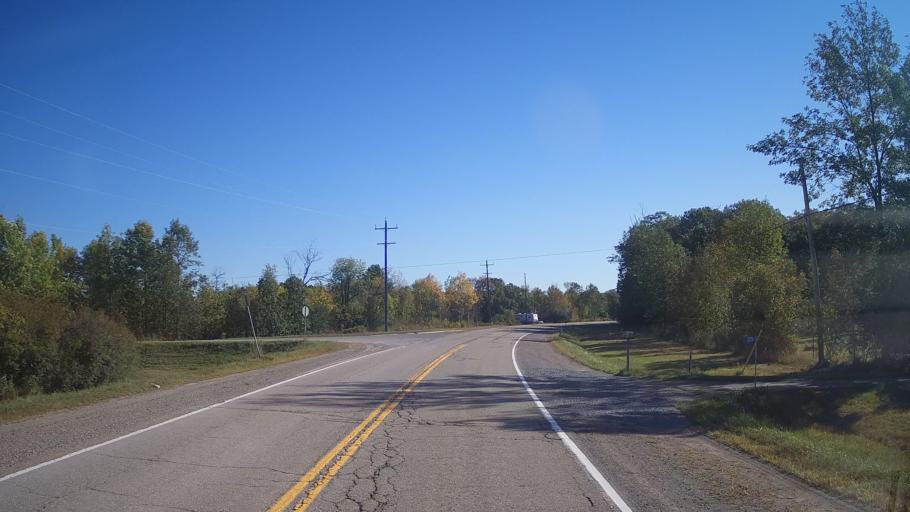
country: CA
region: Ontario
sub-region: Lanark County
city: Smiths Falls
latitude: 44.6251
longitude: -76.0410
